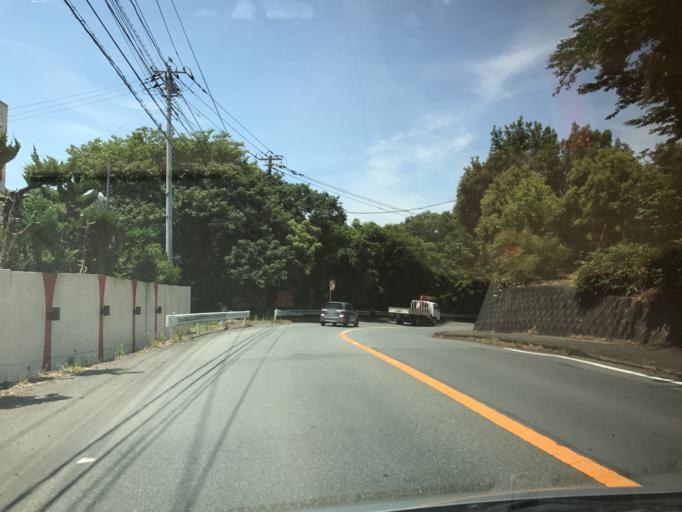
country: JP
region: Shizuoka
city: Numazu
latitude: 35.1446
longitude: 138.8621
